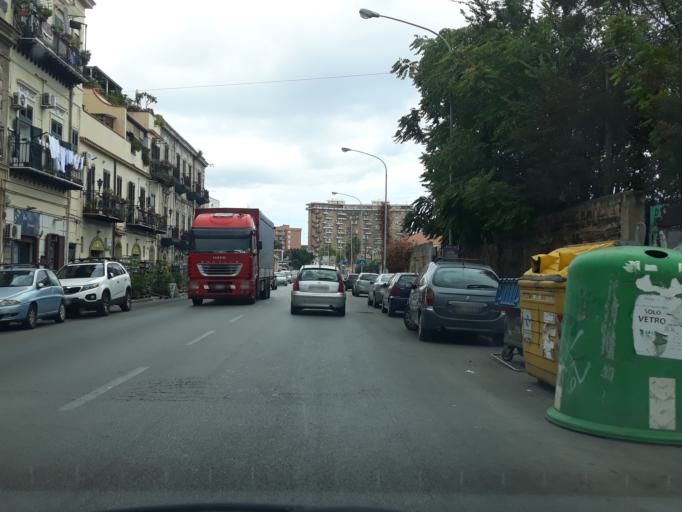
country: IT
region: Sicily
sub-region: Palermo
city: Ciaculli
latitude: 38.1079
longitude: 13.3816
